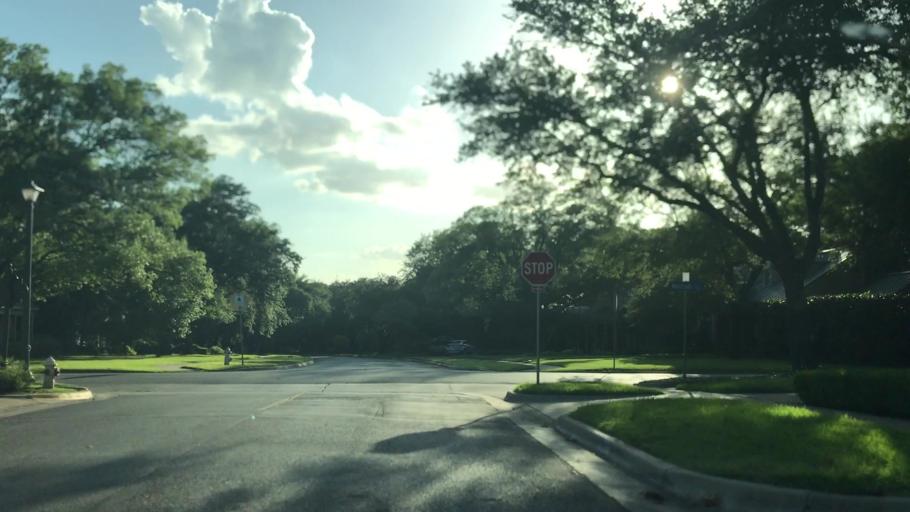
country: US
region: Texas
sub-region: Dallas County
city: University Park
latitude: 32.8323
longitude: -96.8188
